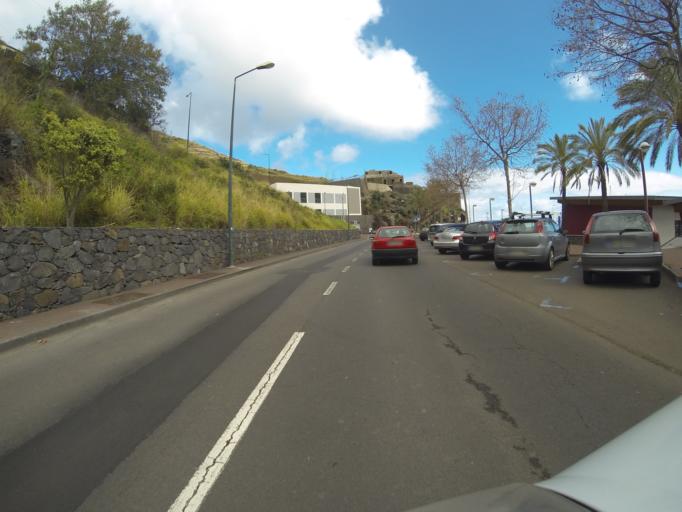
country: PT
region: Madeira
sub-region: Machico
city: Machico
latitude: 32.7188
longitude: -16.7614
